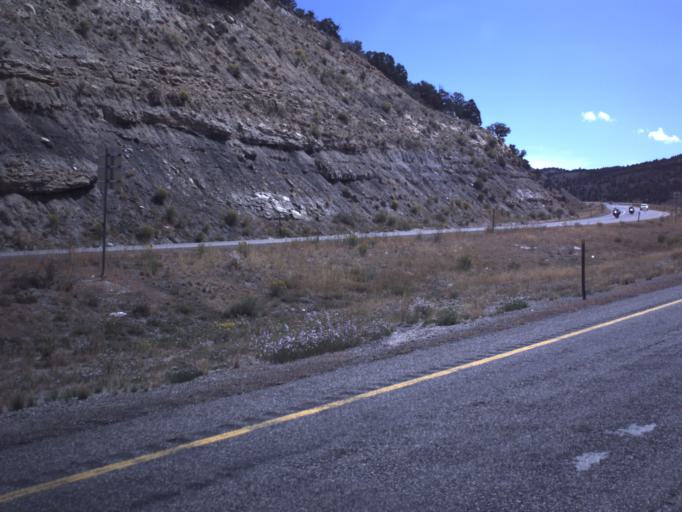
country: US
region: Utah
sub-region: Sevier County
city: Salina
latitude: 38.8123
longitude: -111.5363
